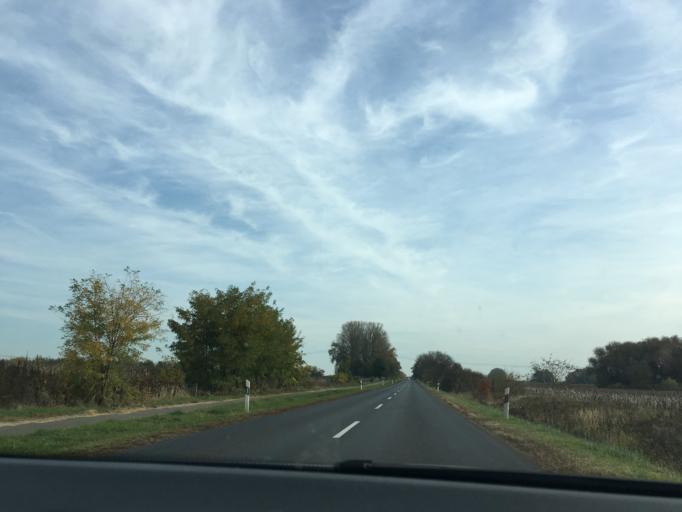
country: HU
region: Szabolcs-Szatmar-Bereg
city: Nagykallo
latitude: 47.8663
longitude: 21.8801
